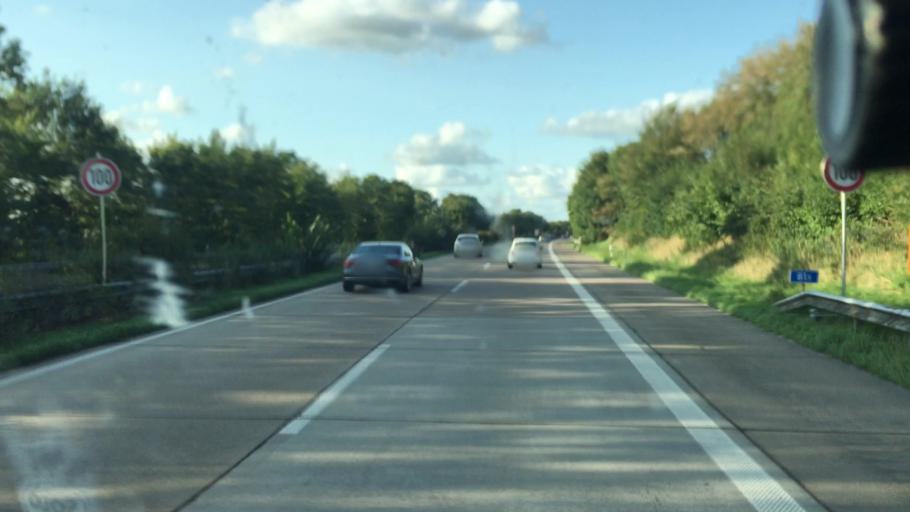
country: DE
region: Lower Saxony
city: Sande
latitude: 53.5031
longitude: 7.9960
